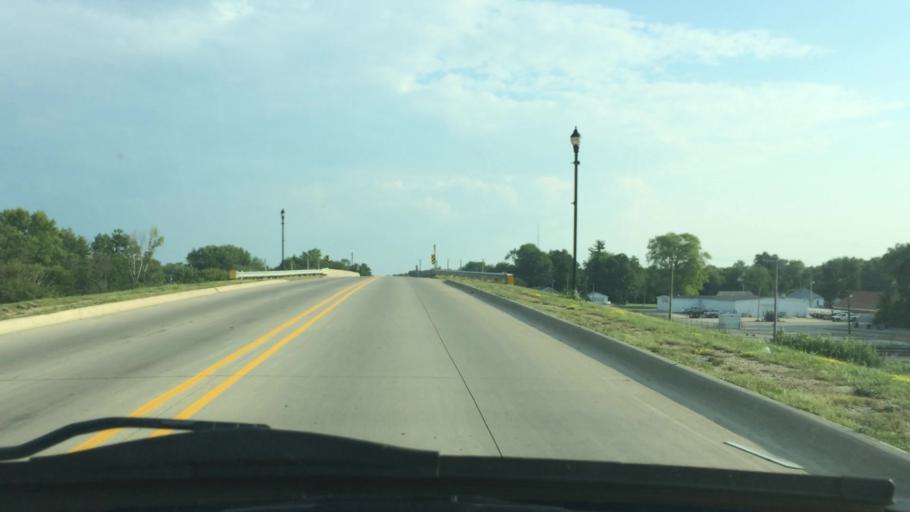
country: US
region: Iowa
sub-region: Henry County
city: Mount Pleasant
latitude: 40.9696
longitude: -91.5386
